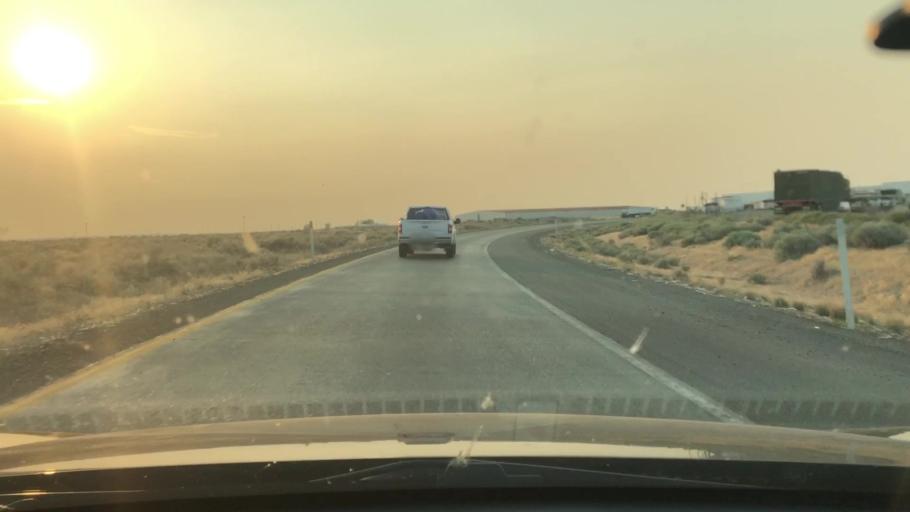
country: US
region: Washington
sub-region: Franklin County
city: Pasco
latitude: 46.2674
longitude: -119.0859
